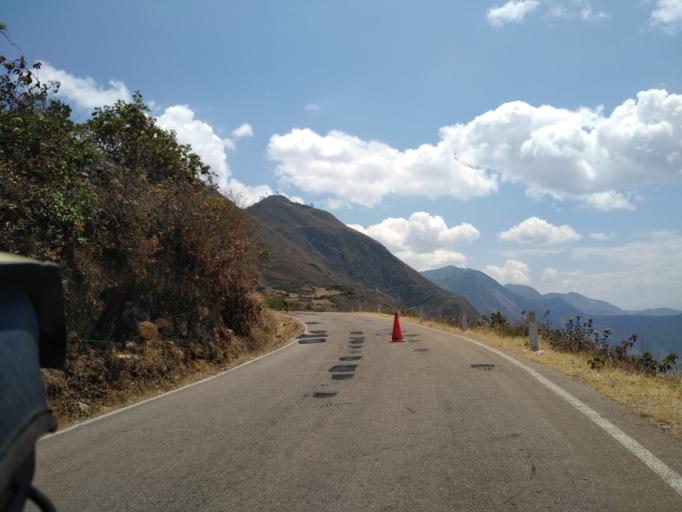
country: PE
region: Cajamarca
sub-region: Provincia de Celendin
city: Celendin
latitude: -6.8851
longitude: -78.1009
